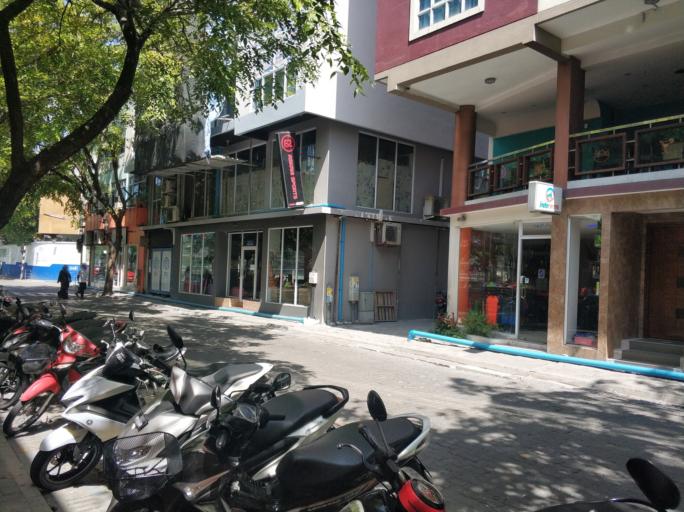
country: MV
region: Maale
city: Male
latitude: 4.1717
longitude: 73.5075
